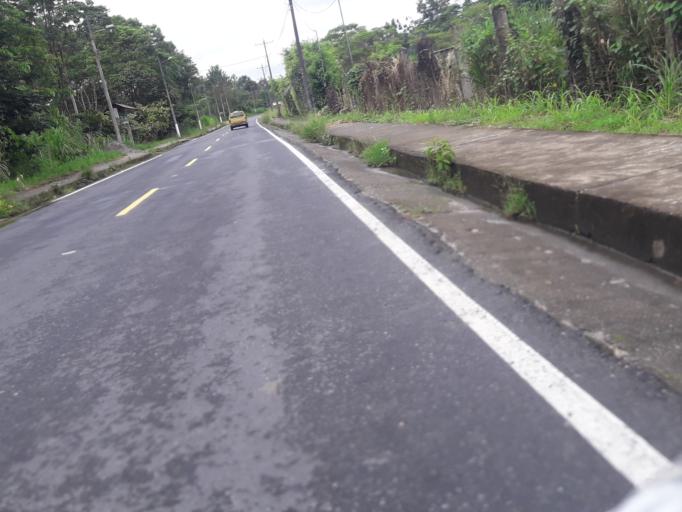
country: EC
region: Napo
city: Tena
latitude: -0.9618
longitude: -77.8580
